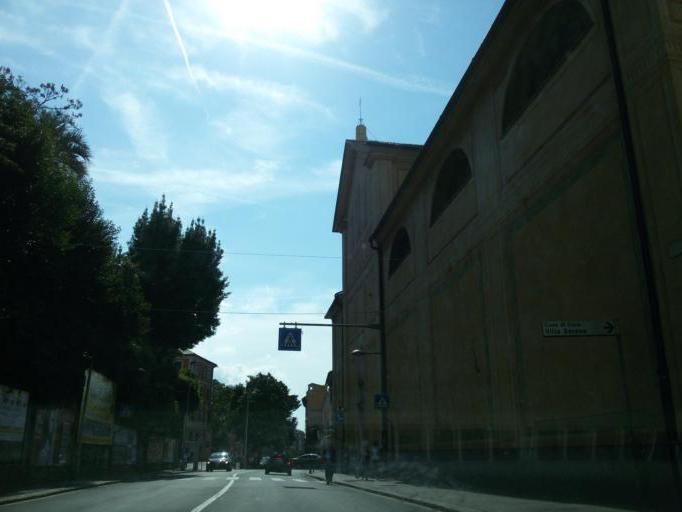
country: IT
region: Liguria
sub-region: Provincia di Genova
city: Genoa
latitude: 44.3998
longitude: 8.9601
